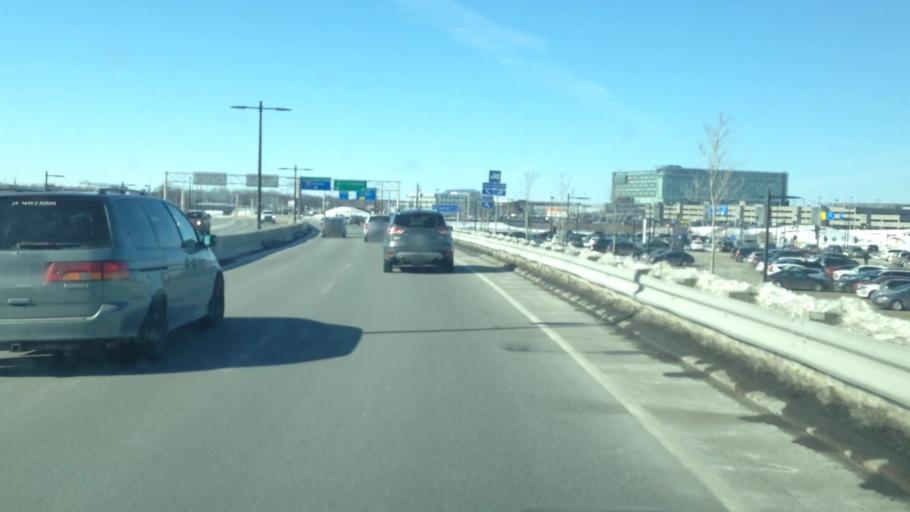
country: CA
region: Quebec
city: Dorval
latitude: 45.4526
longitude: -73.7432
